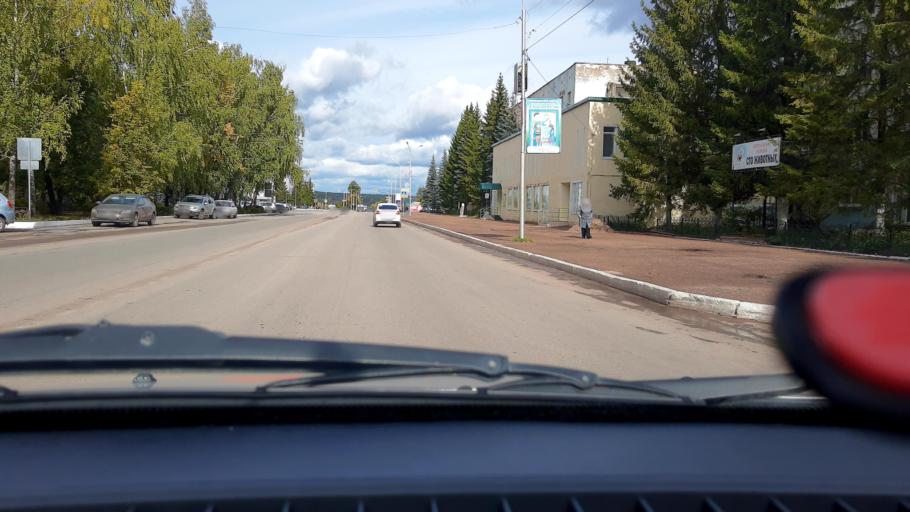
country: RU
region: Bashkortostan
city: Belebey
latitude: 54.1015
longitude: 54.1087
